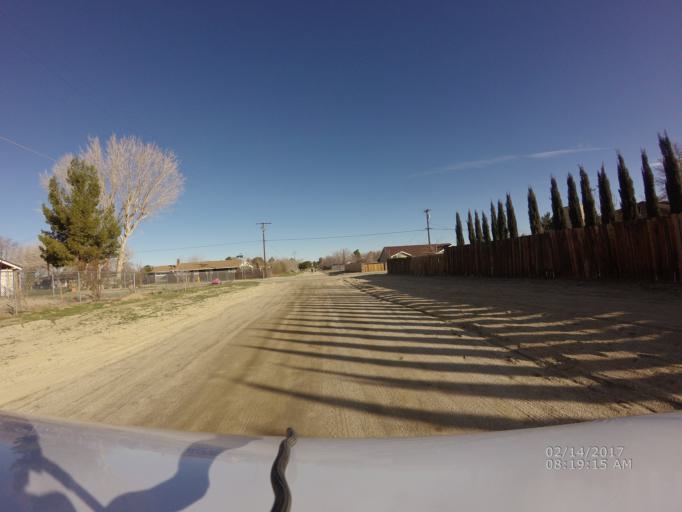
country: US
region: California
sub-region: Los Angeles County
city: Littlerock
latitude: 34.5462
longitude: -117.9538
